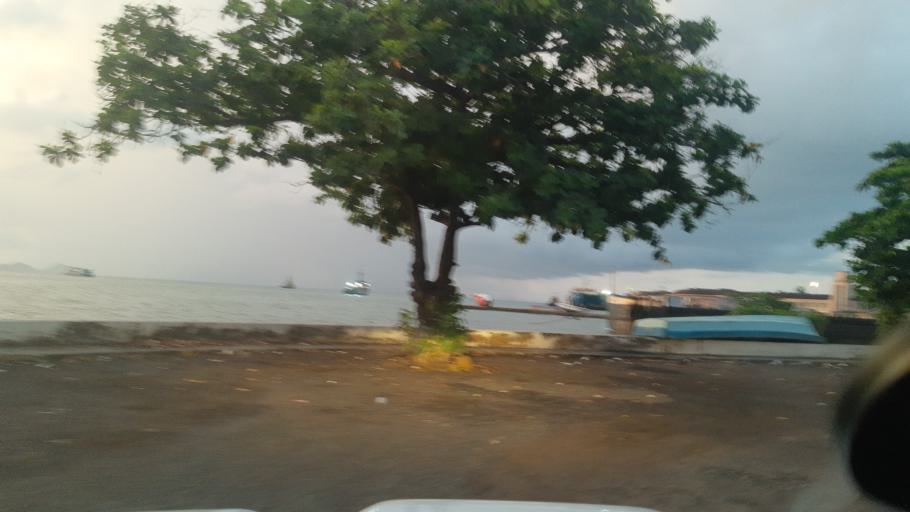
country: ST
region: Sao Tome Island
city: Sao Tome
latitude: 0.3437
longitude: 6.7353
